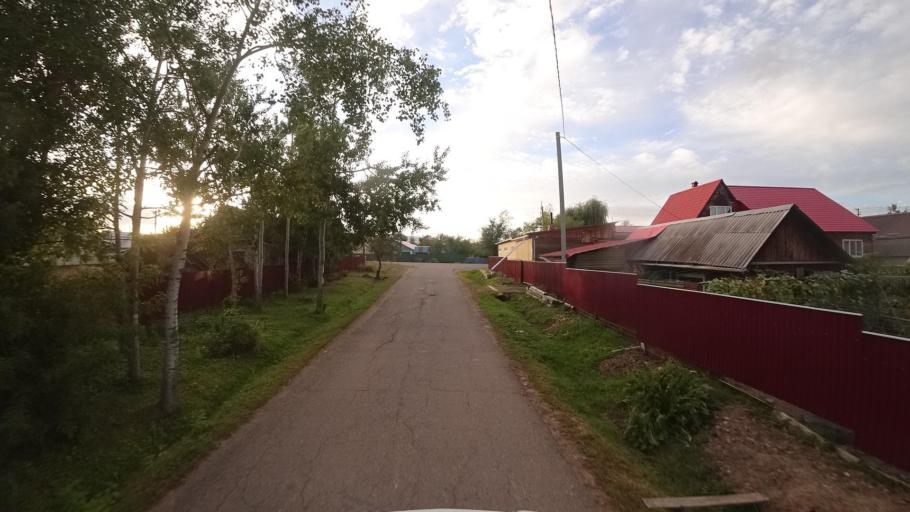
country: RU
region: Primorskiy
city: Yakovlevka
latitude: 44.4223
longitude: 133.4721
